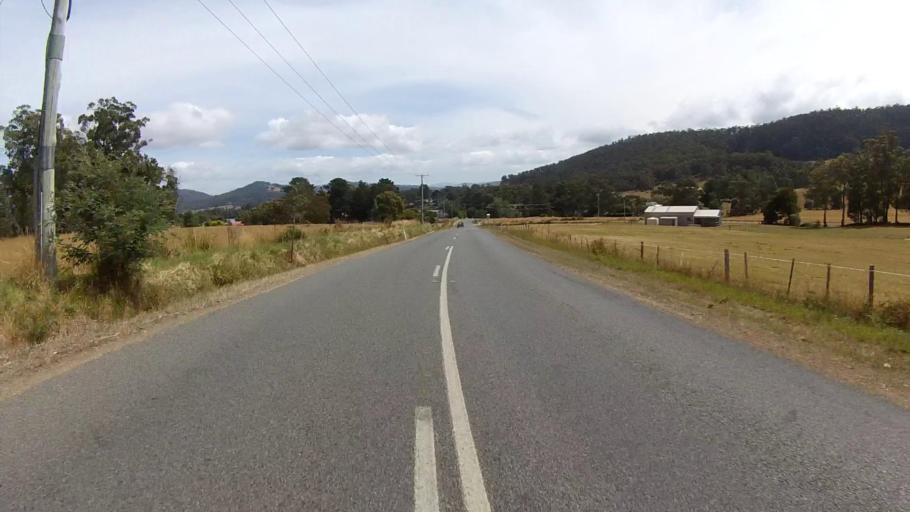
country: AU
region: Tasmania
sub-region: Huon Valley
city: Cygnet
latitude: -43.2138
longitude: 147.1180
